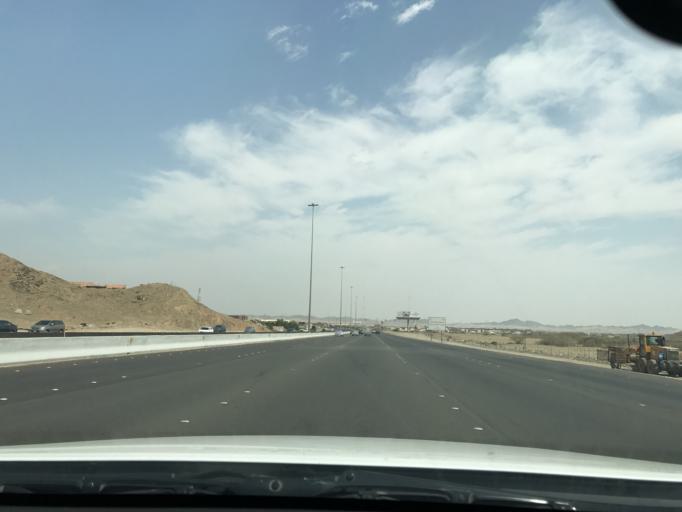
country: SA
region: Makkah
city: Jeddah
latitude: 21.3981
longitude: 39.4077
